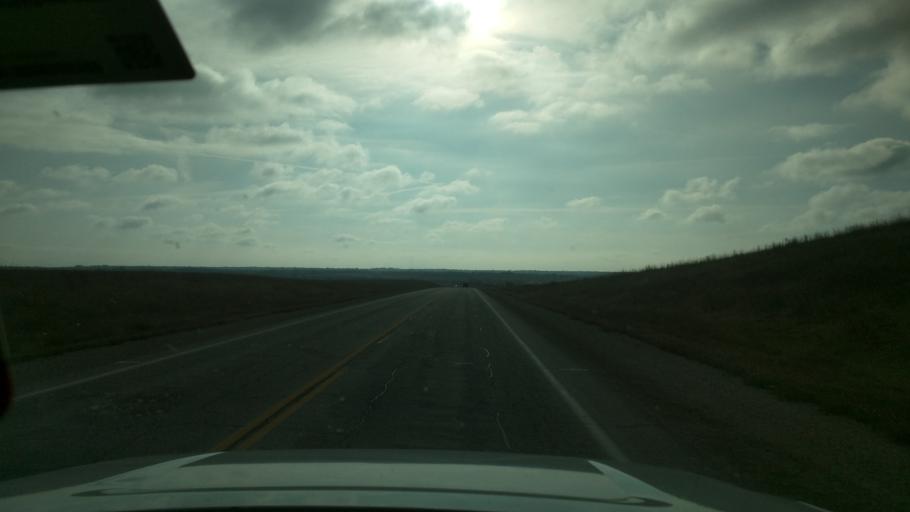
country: US
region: Kansas
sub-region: Chautauqua County
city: Sedan
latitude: 37.0930
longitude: -96.2281
